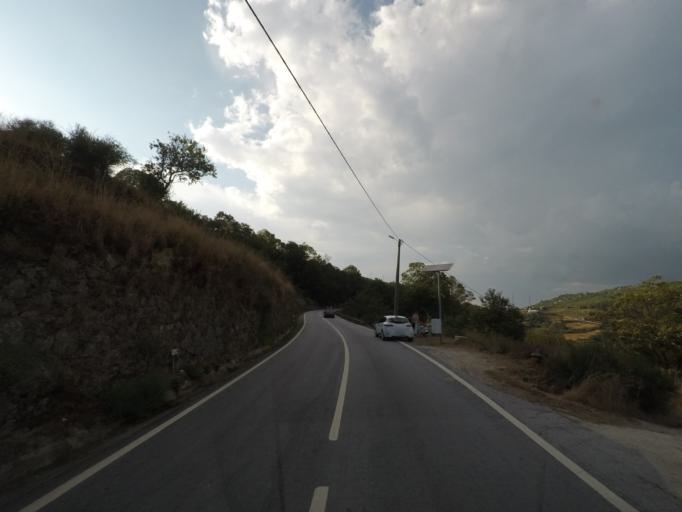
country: PT
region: Porto
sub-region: Baiao
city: Valadares
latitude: 41.1893
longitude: -7.9433
